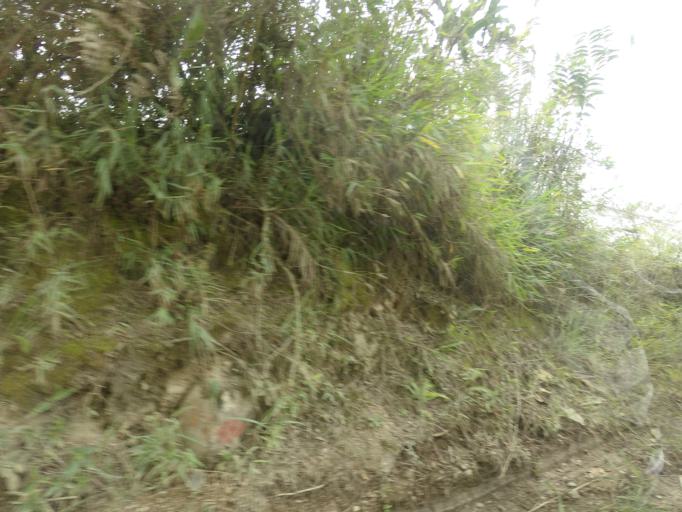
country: CO
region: Huila
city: San Agustin
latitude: 1.9283
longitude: -76.3015
